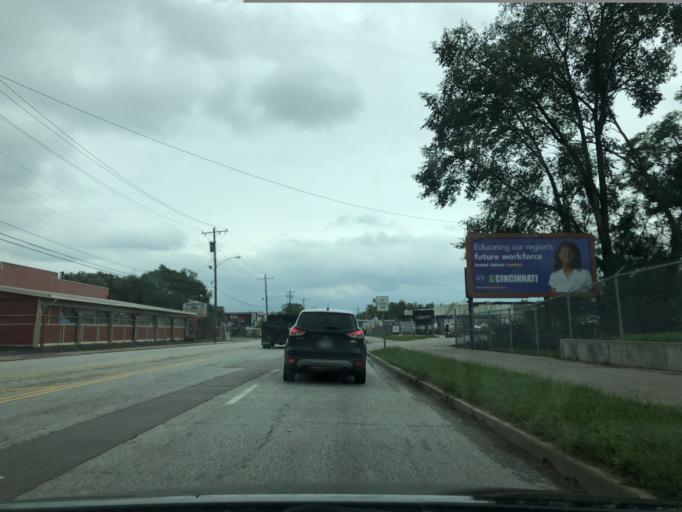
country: US
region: Kentucky
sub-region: Campbell County
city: Dayton
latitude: 39.1122
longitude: -84.4394
